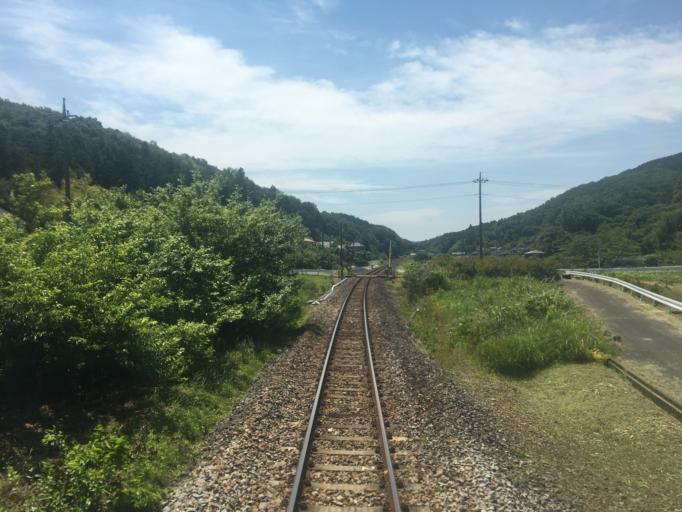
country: JP
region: Saitama
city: Ogawa
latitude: 36.0417
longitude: 139.2634
